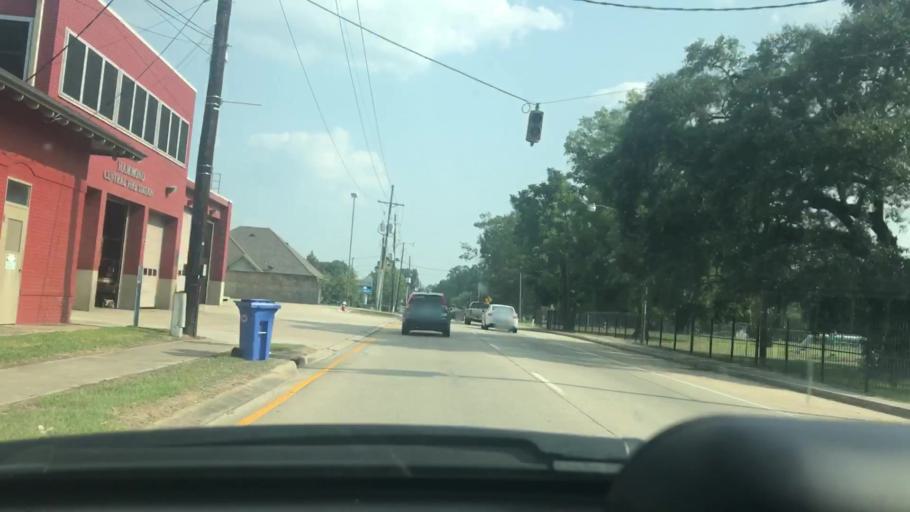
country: US
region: Louisiana
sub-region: Tangipahoa Parish
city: Hammond
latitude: 30.5008
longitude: -90.4614
